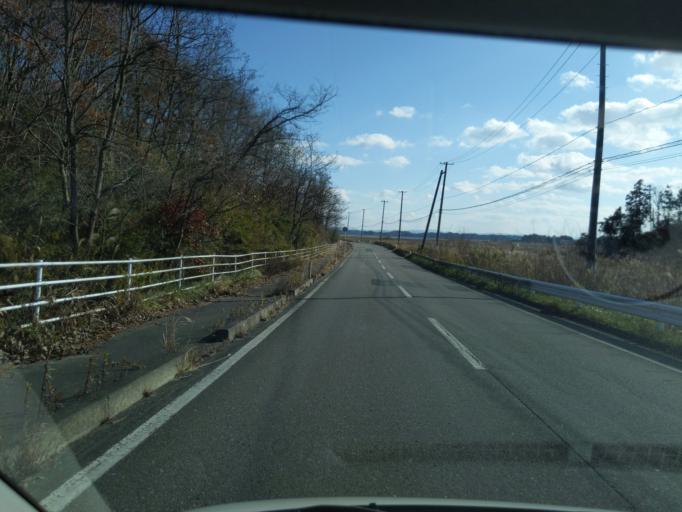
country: JP
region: Miyagi
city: Kogota
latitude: 38.7273
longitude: 141.0668
